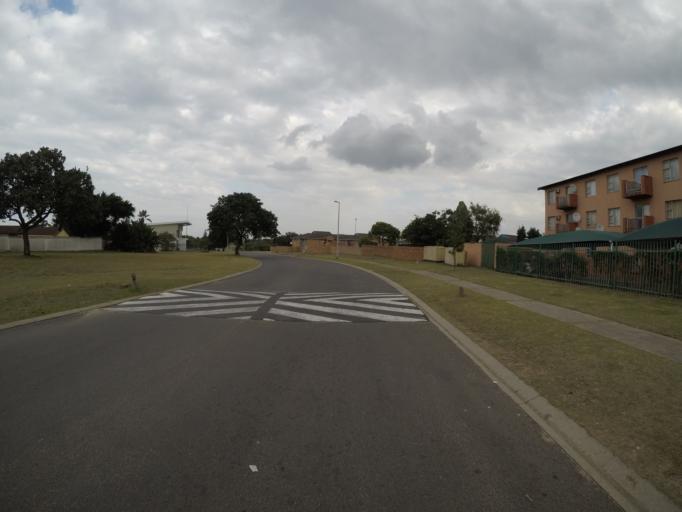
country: ZA
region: KwaZulu-Natal
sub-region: uThungulu District Municipality
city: Richards Bay
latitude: -28.7313
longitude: 32.0510
